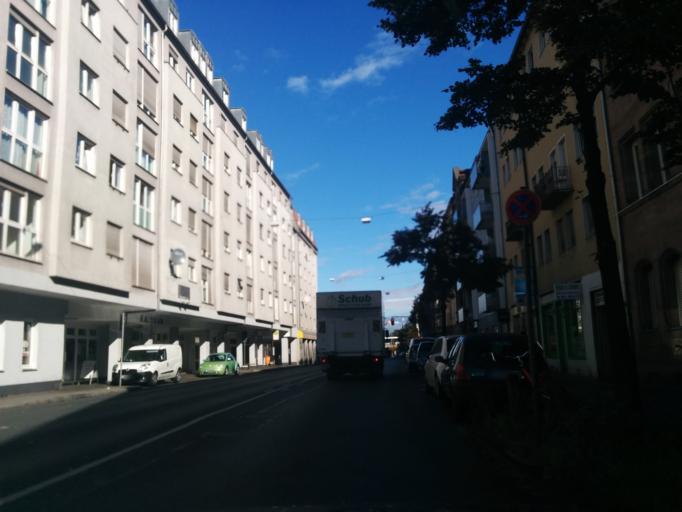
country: DE
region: Bavaria
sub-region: Regierungsbezirk Mittelfranken
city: Nuernberg
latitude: 49.4450
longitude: 11.0976
